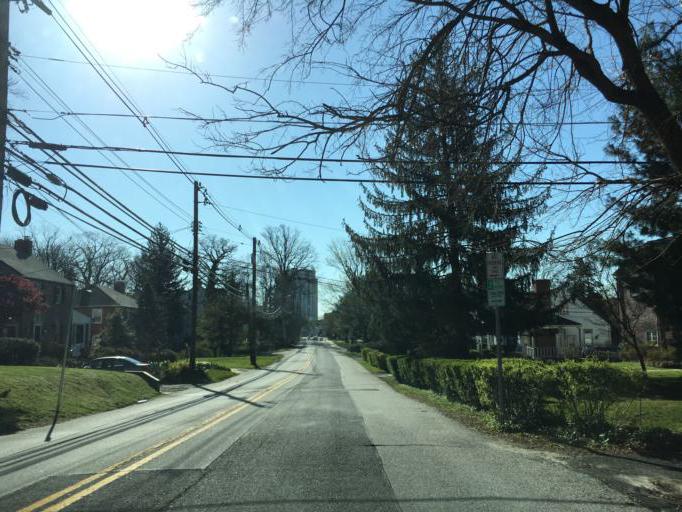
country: US
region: Maryland
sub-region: Baltimore County
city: Towson
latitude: 39.4053
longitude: -76.6117
